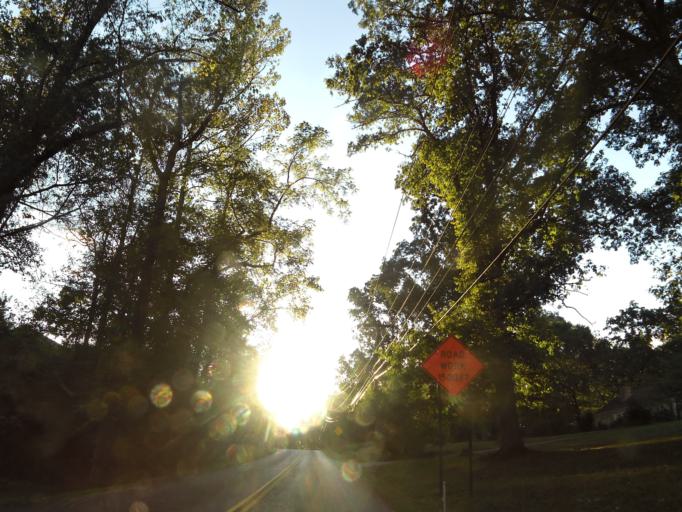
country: US
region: Tennessee
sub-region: Knox County
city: Knoxville
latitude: 35.9059
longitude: -83.9461
